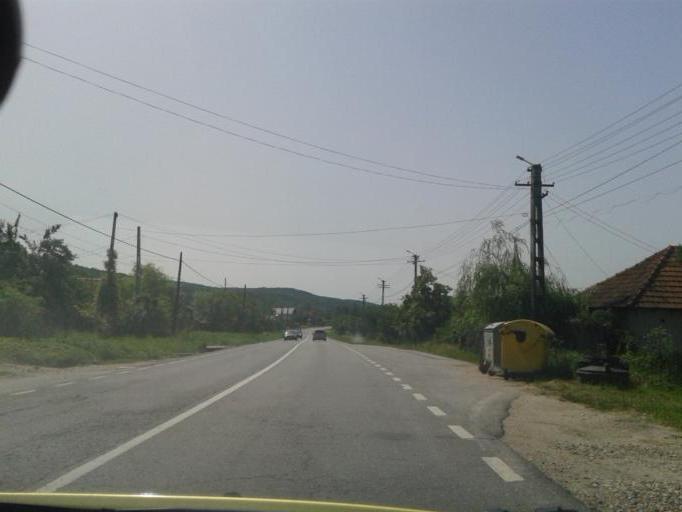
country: RO
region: Arges
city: Draganu-Olteni
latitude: 44.9345
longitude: 24.7094
